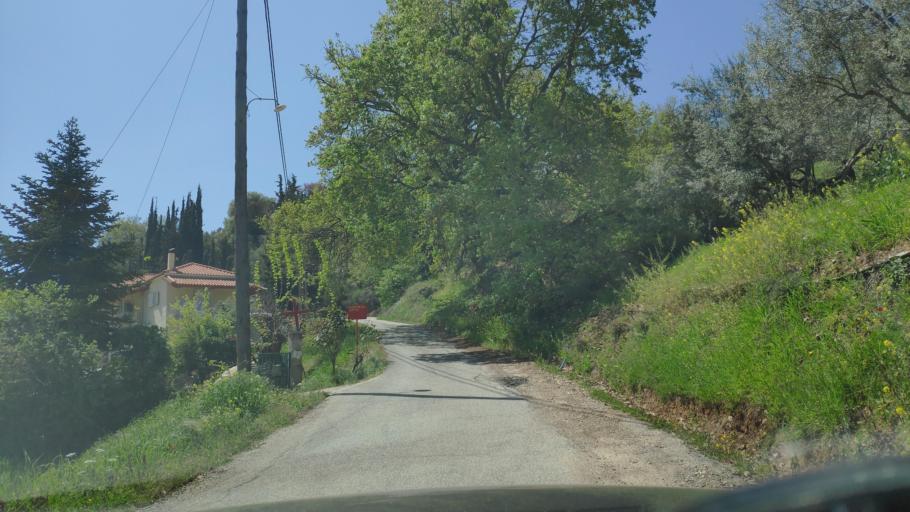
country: GR
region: West Greece
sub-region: Nomos Achaias
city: Aiyira
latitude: 38.0781
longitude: 22.3386
